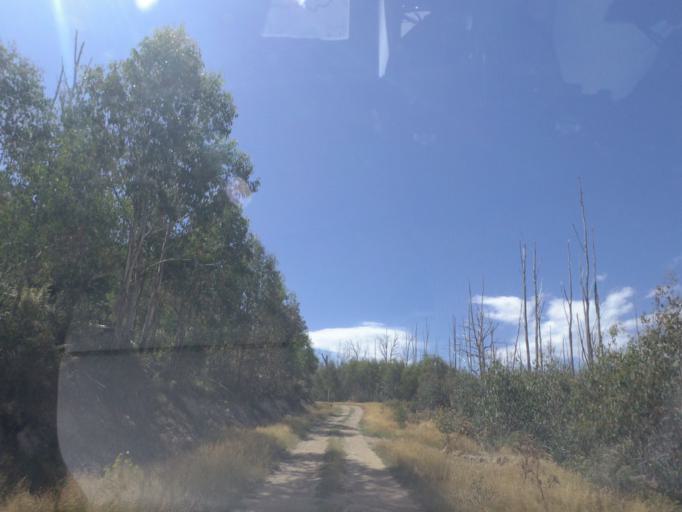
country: AU
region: Victoria
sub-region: Murrindindi
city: Alexandra
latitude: -37.4652
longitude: 145.8490
